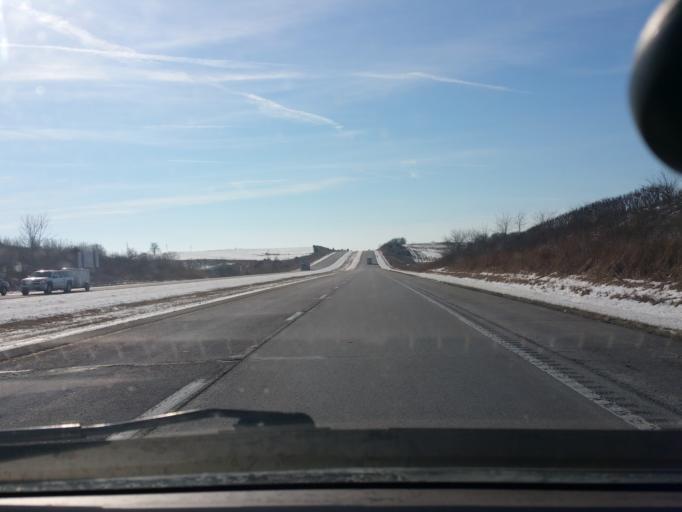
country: US
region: Iowa
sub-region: Decatur County
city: Lamoni
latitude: 40.5068
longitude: -93.9657
